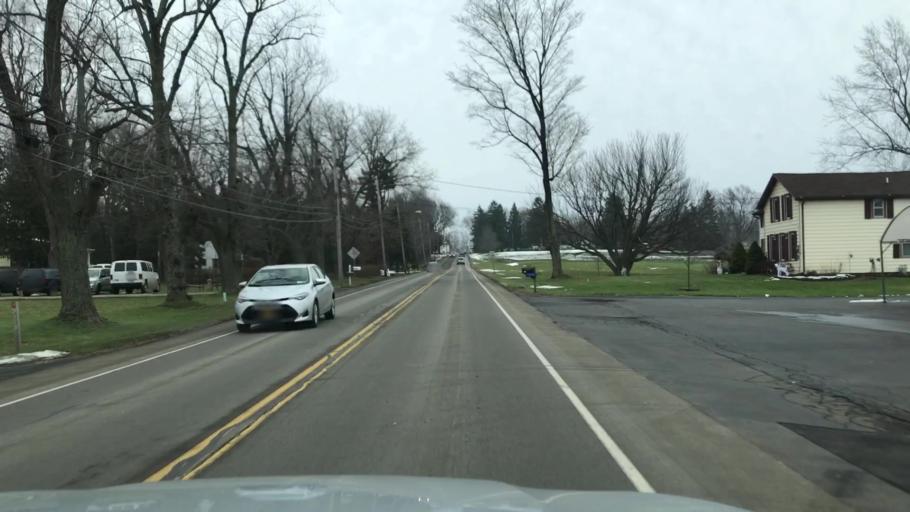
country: US
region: New York
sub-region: Erie County
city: Hamburg
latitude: 42.7444
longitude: -78.8034
